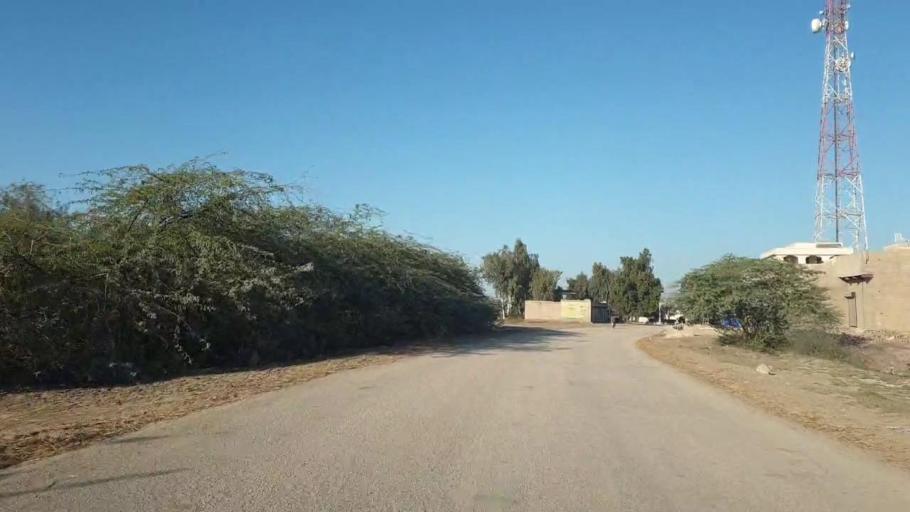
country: PK
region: Sindh
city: Dokri
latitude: 27.3675
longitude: 68.1161
